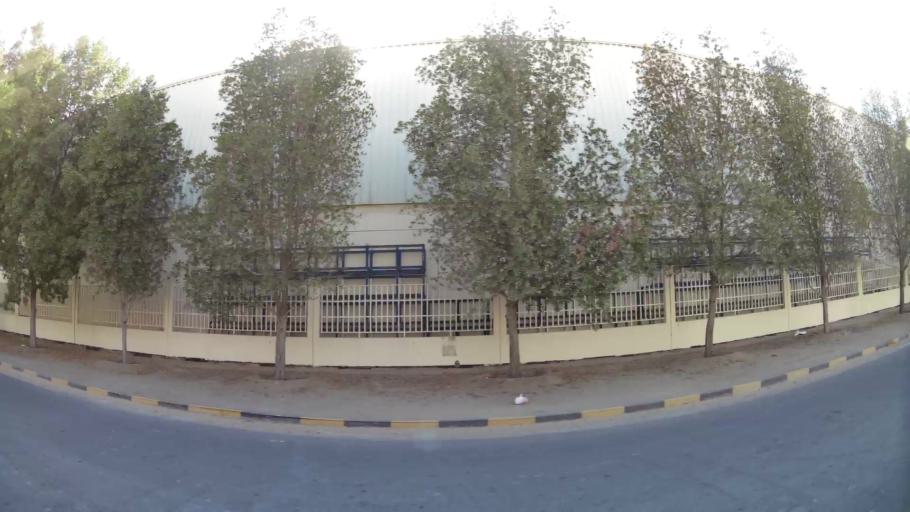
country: AE
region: Dubai
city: Dubai
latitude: 24.9884
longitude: 55.1092
